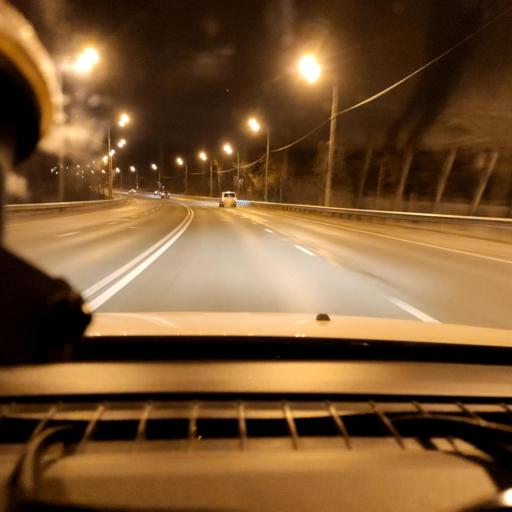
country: RU
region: Samara
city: Samara
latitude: 53.3034
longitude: 50.2263
